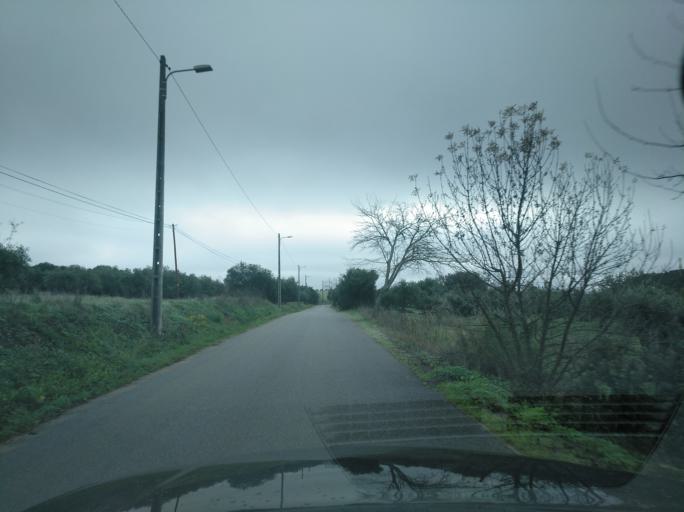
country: PT
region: Portalegre
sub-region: Elvas
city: Elvas
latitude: 38.8640
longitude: -7.1648
